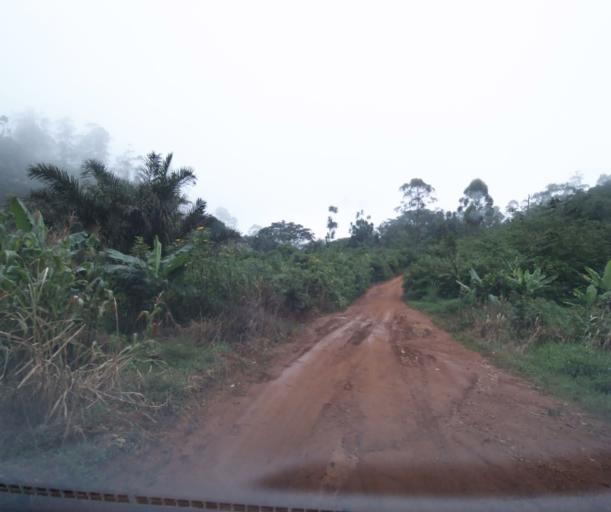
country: CM
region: West
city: Dschang
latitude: 5.5171
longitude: 9.9825
